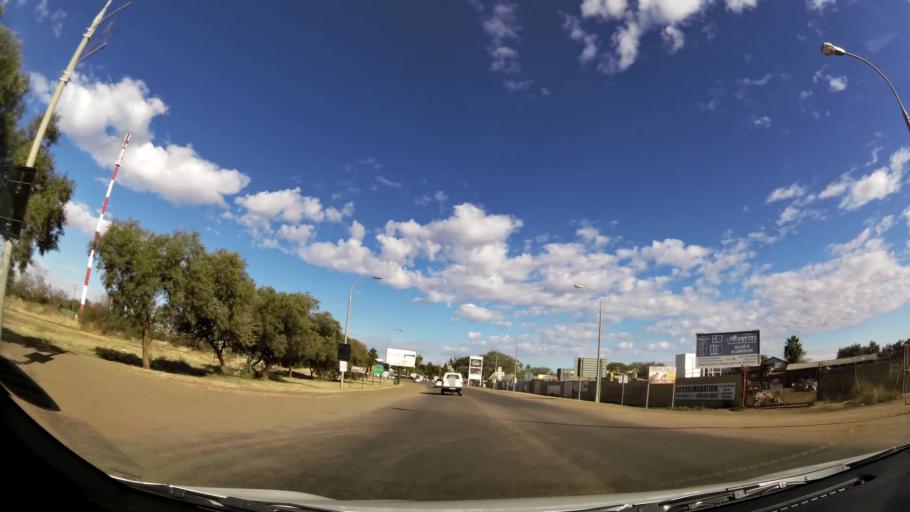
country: ZA
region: Limpopo
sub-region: Waterberg District Municipality
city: Bela-Bela
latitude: -24.8915
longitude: 28.2976
